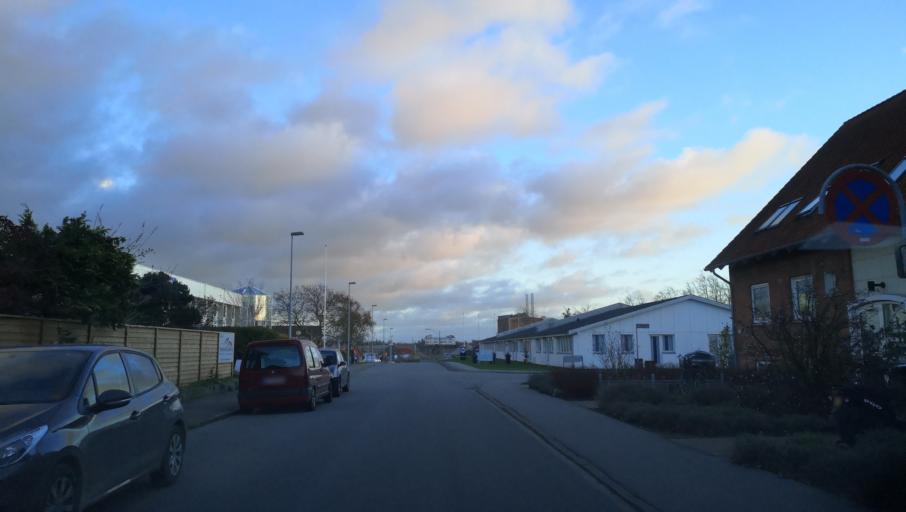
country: DK
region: Zealand
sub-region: Naestved Kommune
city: Naestved
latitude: 55.2266
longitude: 11.7483
